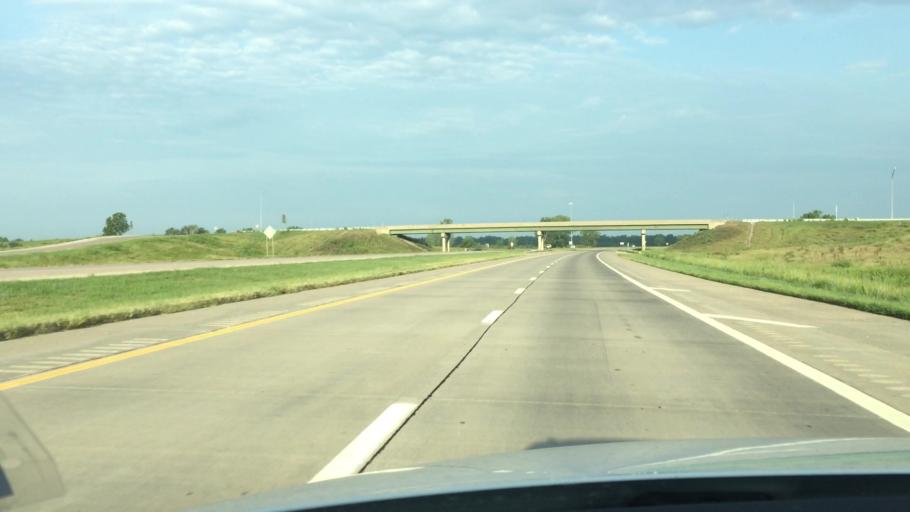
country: US
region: Kansas
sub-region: Doniphan County
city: Elwood
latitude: 39.7416
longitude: -94.8912
